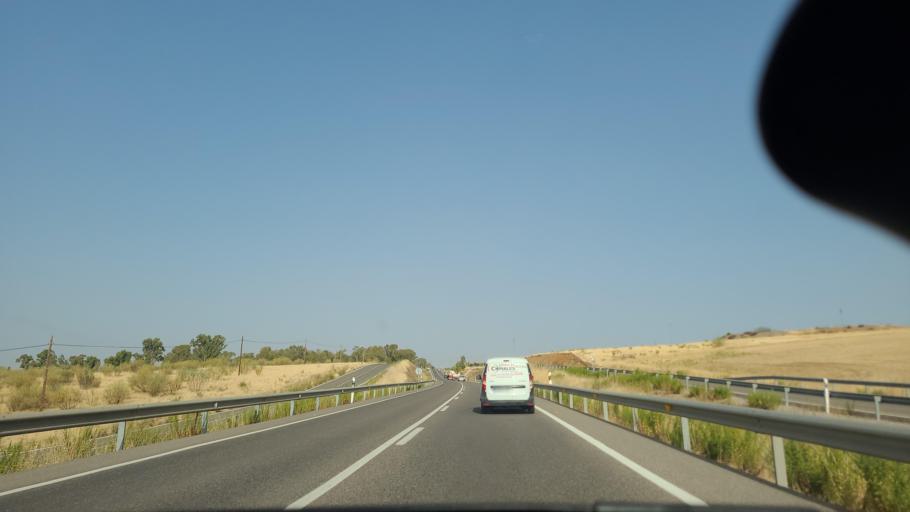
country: ES
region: Andalusia
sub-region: Province of Cordoba
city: Penarroya-Pueblonuevo
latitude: 38.2954
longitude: -5.2389
